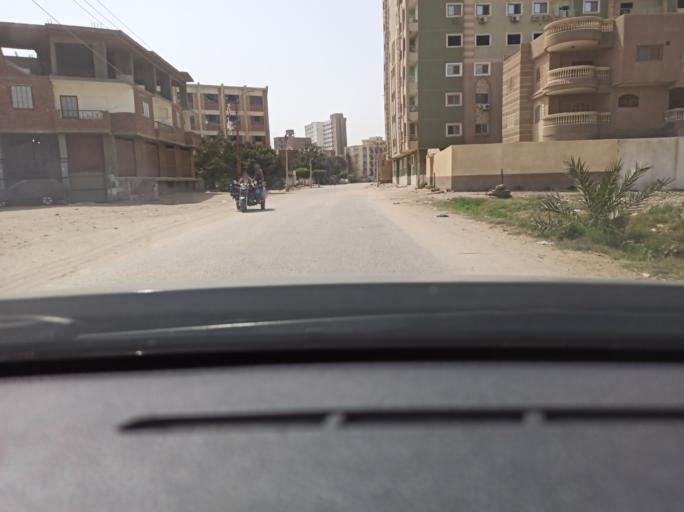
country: EG
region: Muhafazat Bani Suwayf
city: Bani Suwayf
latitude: 29.0848
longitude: 31.0935
